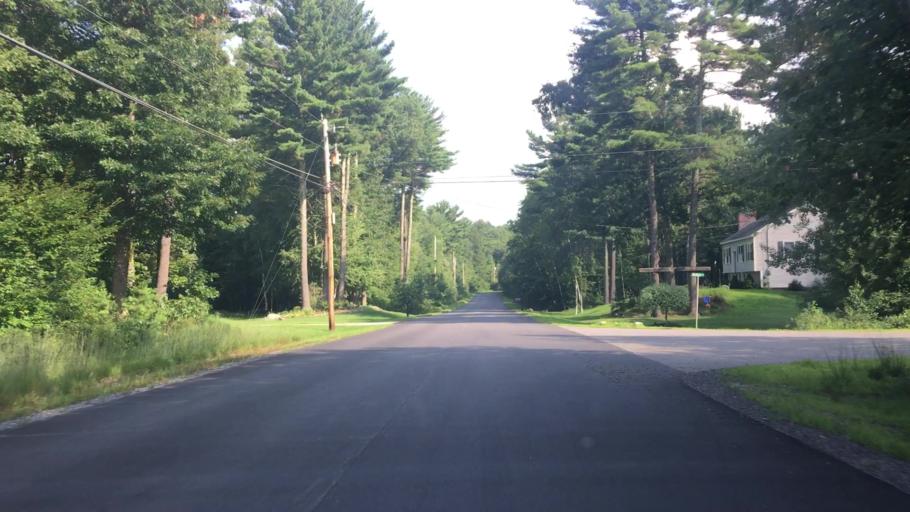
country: US
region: New Hampshire
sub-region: Rockingham County
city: Derry Village
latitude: 42.9362
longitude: -71.3246
